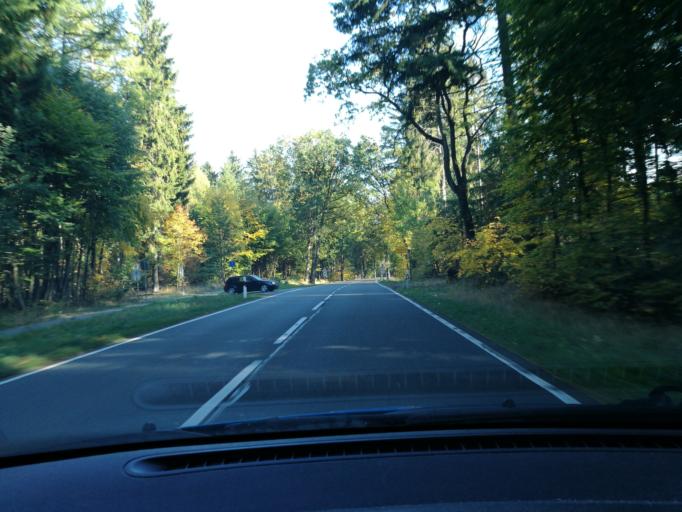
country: DE
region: Lower Saxony
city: Karwitz
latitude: 53.1160
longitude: 11.0019
